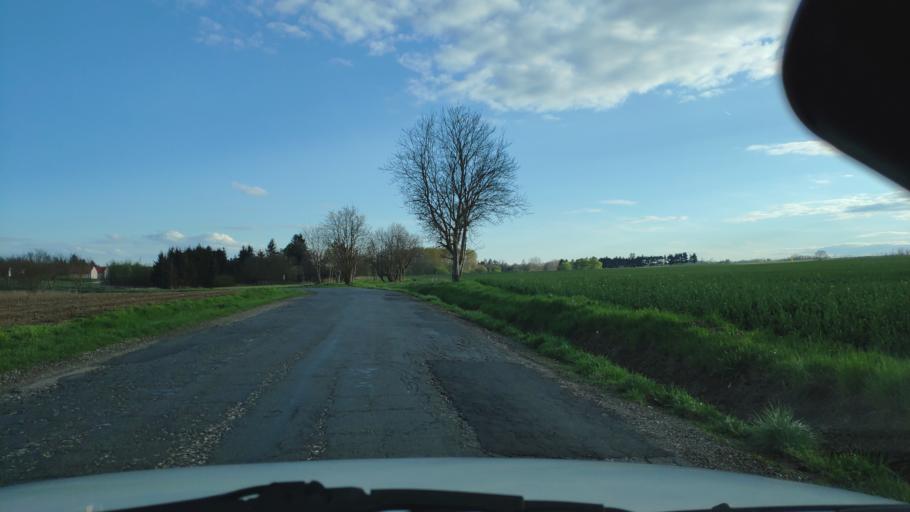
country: HU
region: Zala
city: Zalakomar
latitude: 46.4607
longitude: 17.1253
